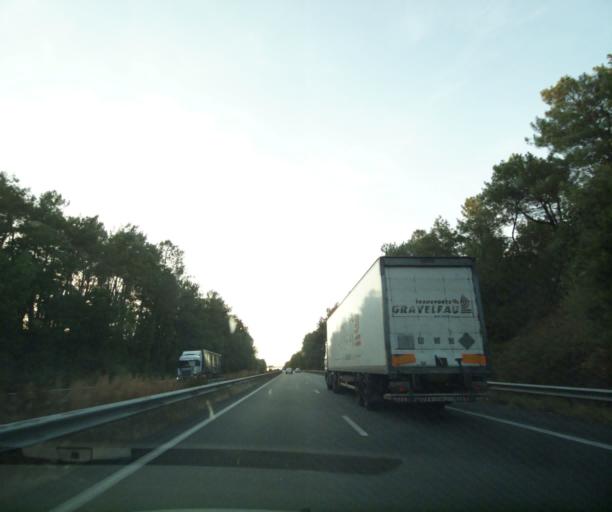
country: FR
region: Aquitaine
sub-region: Departement du Lot-et-Garonne
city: Fourques-sur-Garonne
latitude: 44.4392
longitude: 0.1176
